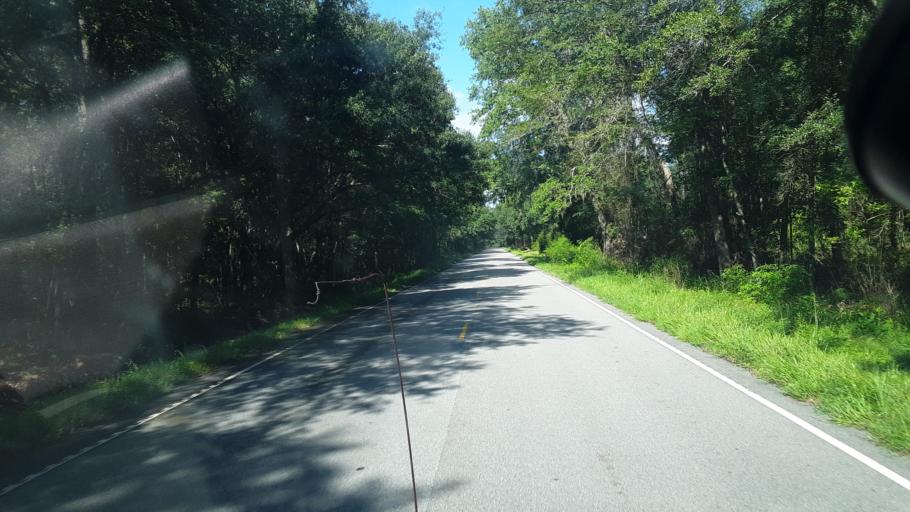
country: US
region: South Carolina
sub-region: Jasper County
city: Ridgeland
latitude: 32.5897
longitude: -80.9563
